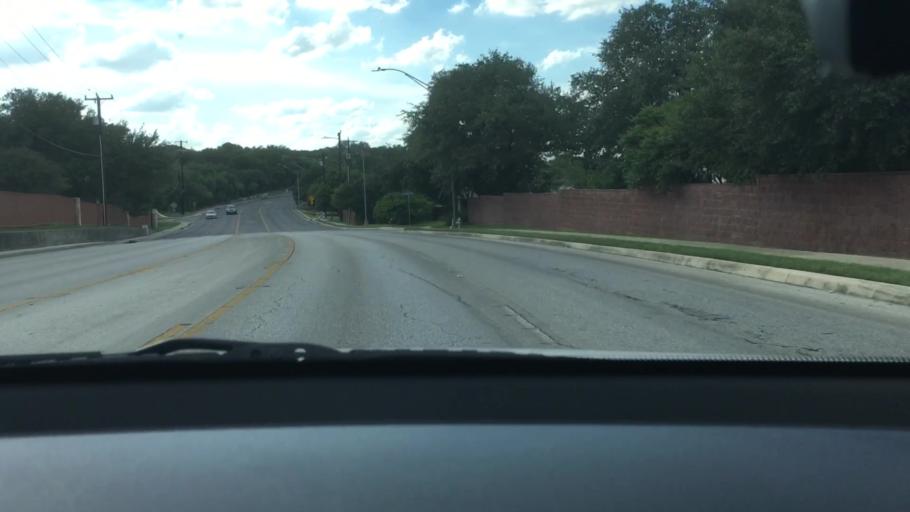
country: US
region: Texas
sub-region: Bexar County
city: Live Oak
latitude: 29.5927
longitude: -98.3986
